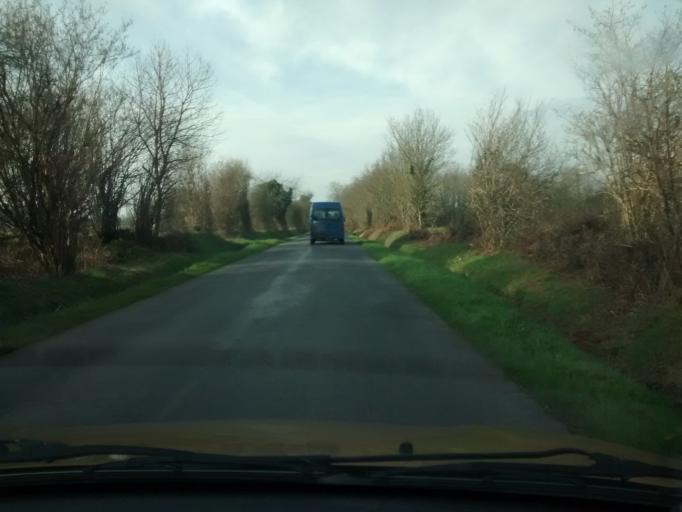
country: FR
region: Pays de la Loire
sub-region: Departement de la Loire-Atlantique
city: Notre-Dame-des-Landes
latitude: 47.3743
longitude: -1.7204
